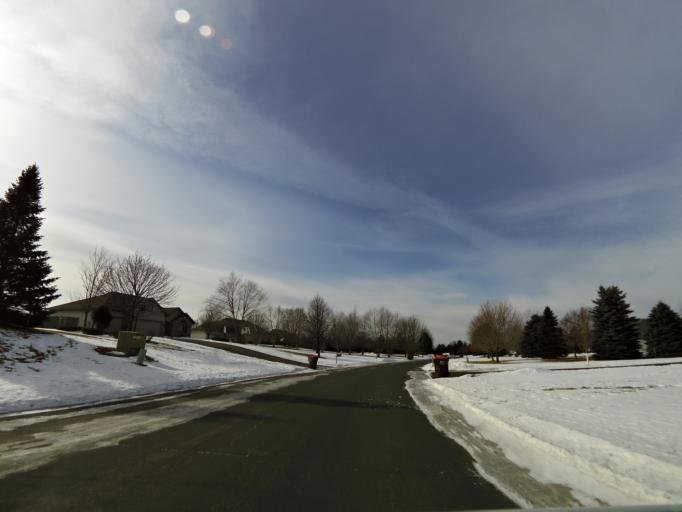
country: US
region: Minnesota
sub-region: Washington County
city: Lake Elmo
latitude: 44.9836
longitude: -92.8550
